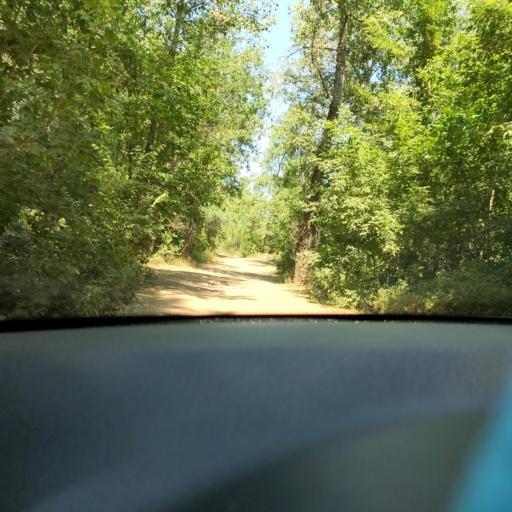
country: RU
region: Samara
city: Smyshlyayevka
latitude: 53.2204
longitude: 50.3440
